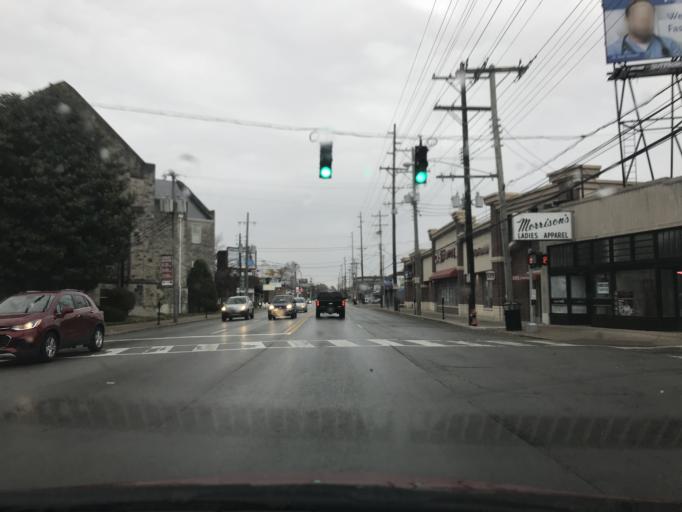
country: US
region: Kentucky
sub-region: Jefferson County
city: Audubon Park
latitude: 38.2244
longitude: -85.6934
